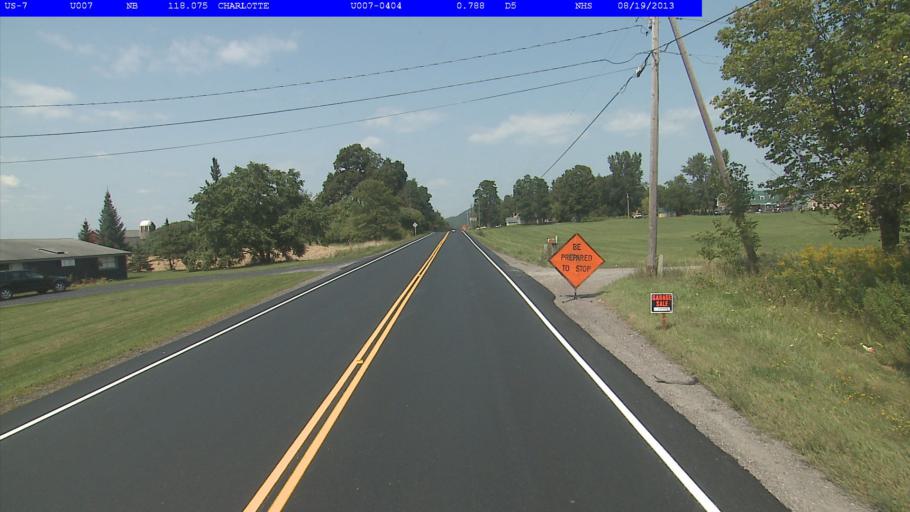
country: US
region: Vermont
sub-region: Addison County
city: Vergennes
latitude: 44.2736
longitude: -73.2341
